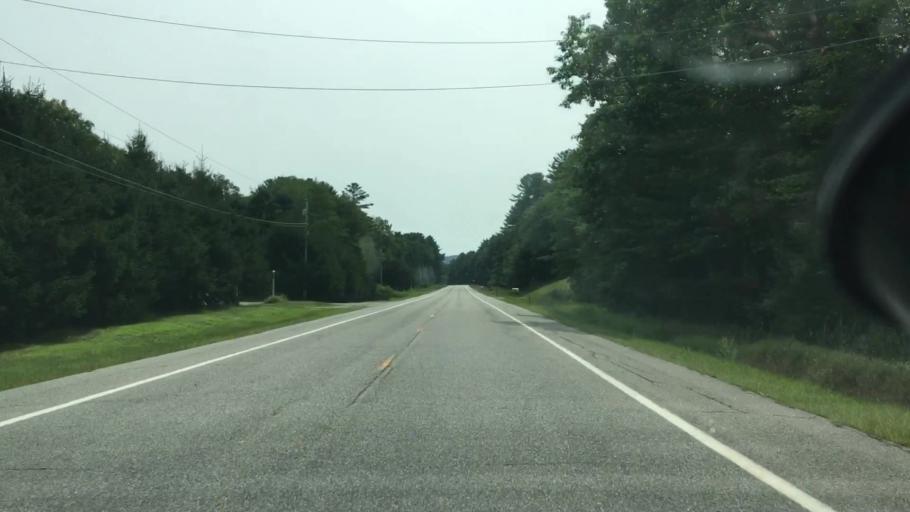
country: US
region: Maine
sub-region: Kennebec County
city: Wayne
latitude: 44.3660
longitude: -70.0894
